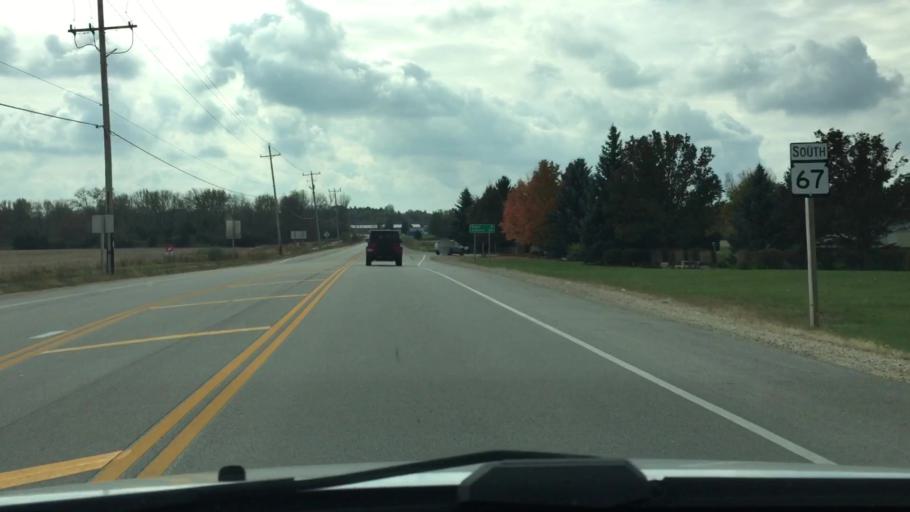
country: US
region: Wisconsin
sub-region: Waukesha County
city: Dousman
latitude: 43.0217
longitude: -88.4625
